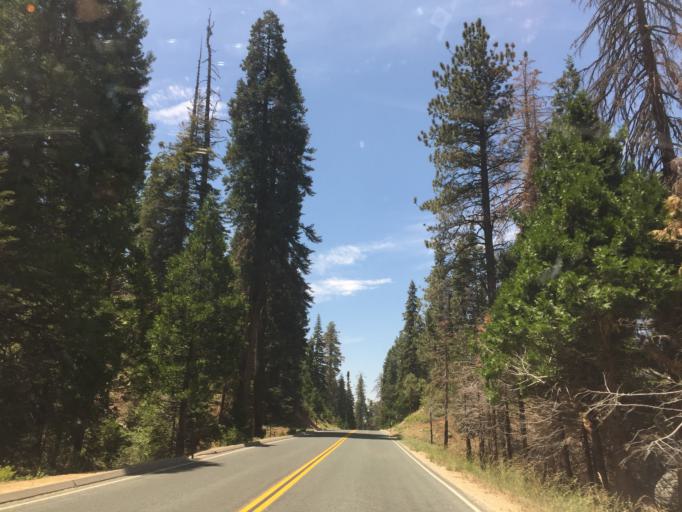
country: US
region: California
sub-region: Fresno County
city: Squaw Valley
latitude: 36.7502
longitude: -118.9647
